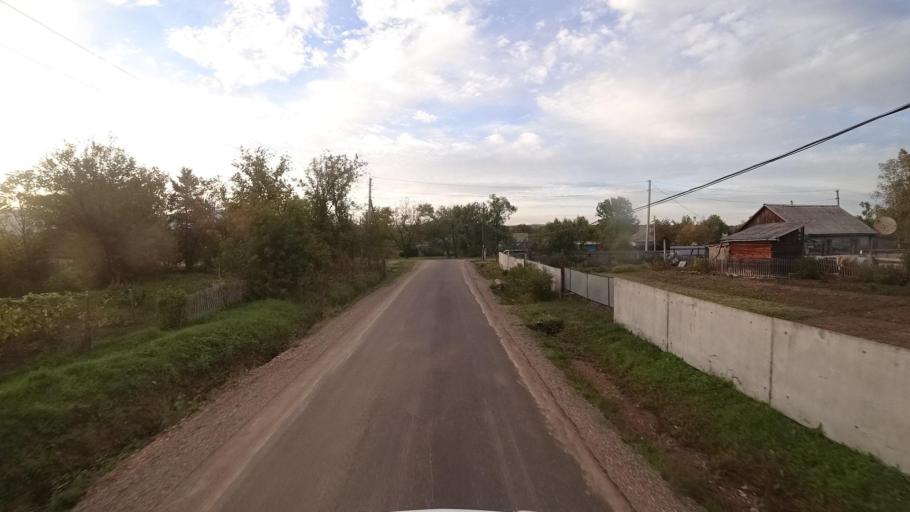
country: RU
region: Primorskiy
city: Yakovlevka
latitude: 44.4236
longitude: 133.4657
